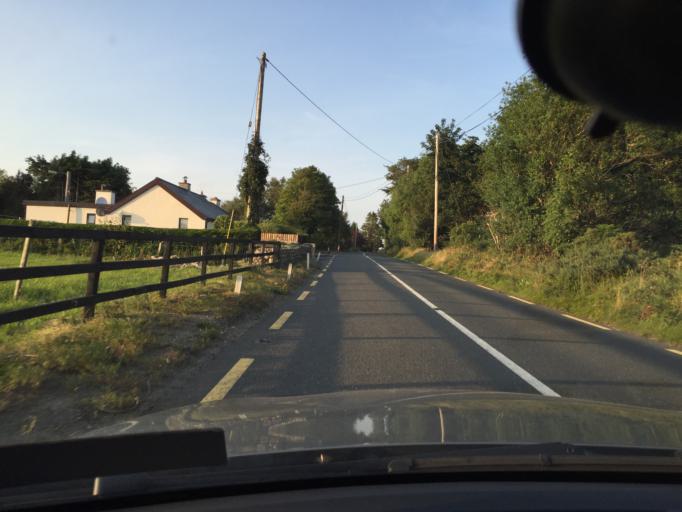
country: IE
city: Newtownmountkennedy
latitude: 53.0831
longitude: -6.2109
